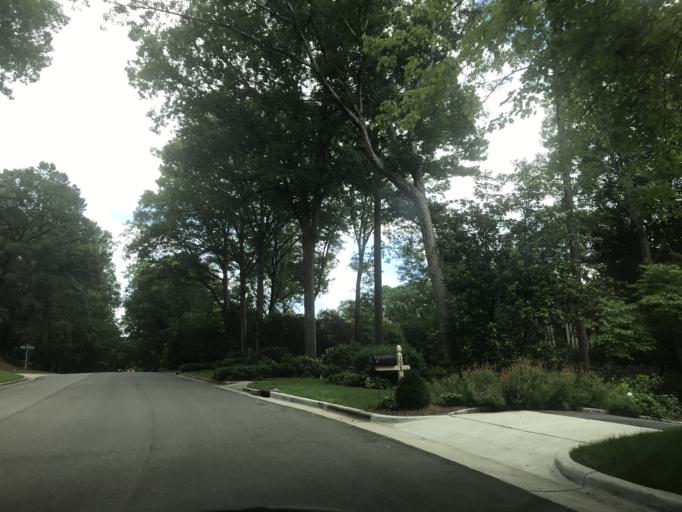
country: US
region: North Carolina
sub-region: Wake County
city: West Raleigh
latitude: 35.8290
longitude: -78.6527
